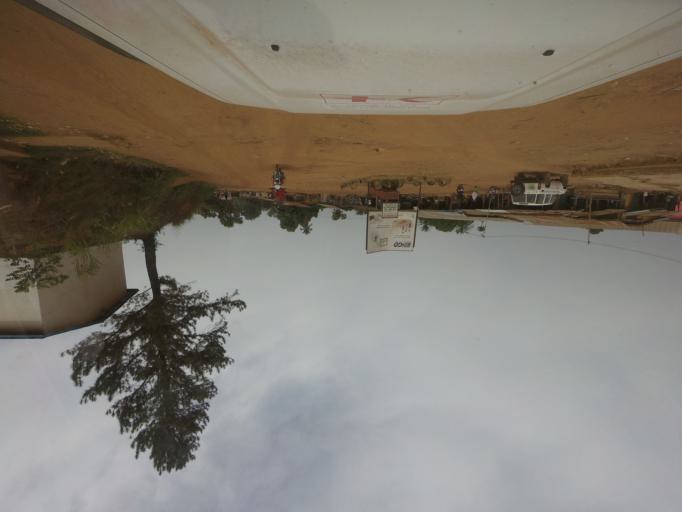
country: SL
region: Eastern Province
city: Buedu
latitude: 8.3599
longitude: -10.2088
